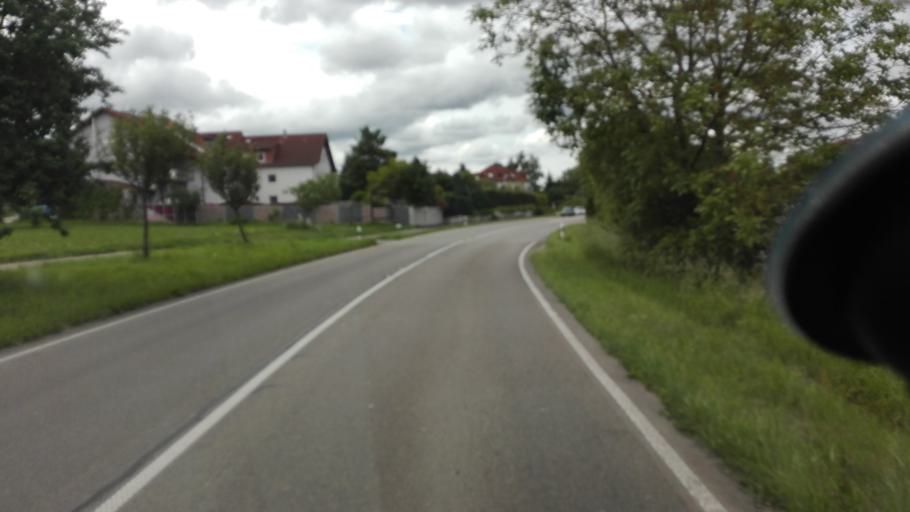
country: DE
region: Baden-Wuerttemberg
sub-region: Karlsruhe Region
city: Kronau
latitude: 49.2261
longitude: 8.6555
